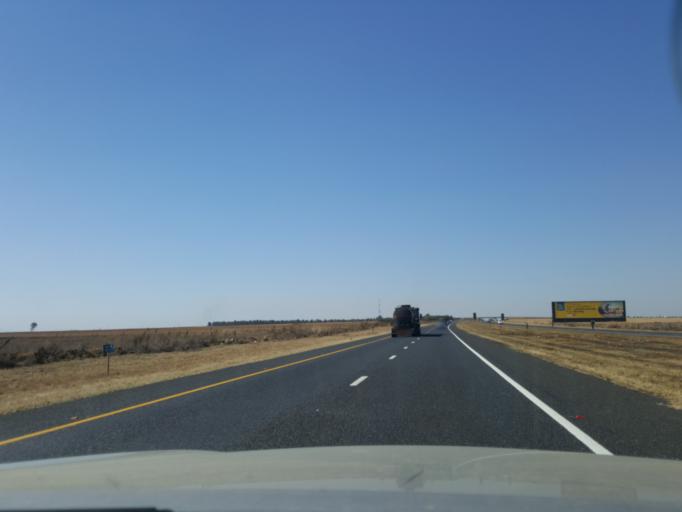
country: ZA
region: Mpumalanga
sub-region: Nkangala District Municipality
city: Delmas
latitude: -26.0727
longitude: 28.7429
